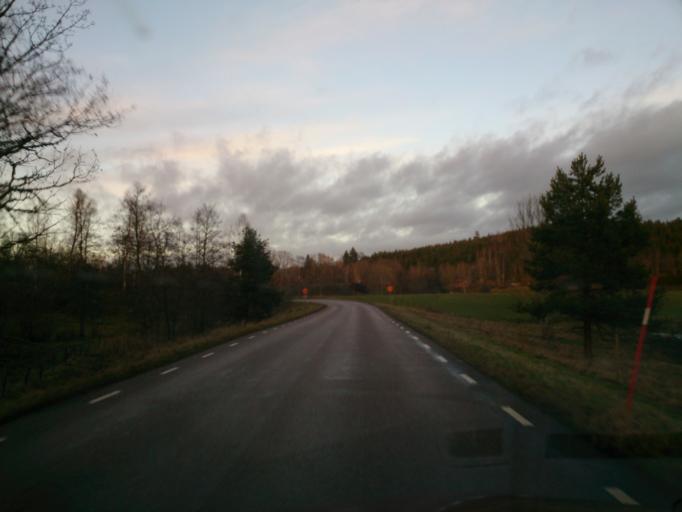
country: SE
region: OEstergoetland
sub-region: Atvidabergs Kommun
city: Atvidaberg
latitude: 58.3316
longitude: 16.0280
